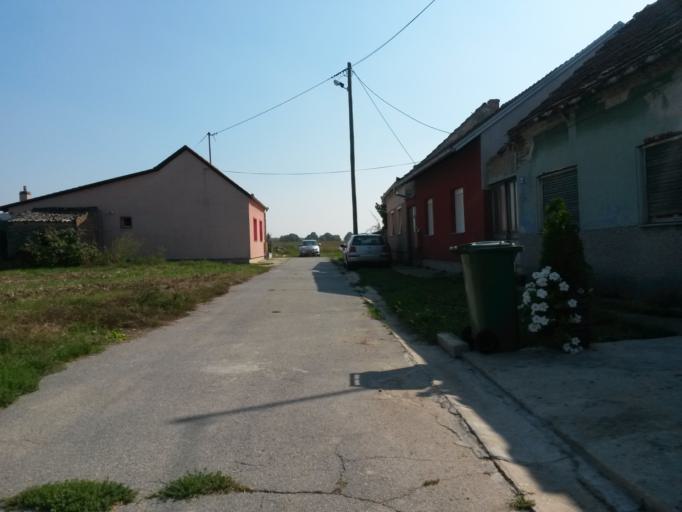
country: HR
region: Osjecko-Baranjska
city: Brijest
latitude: 45.5413
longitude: 18.6672
